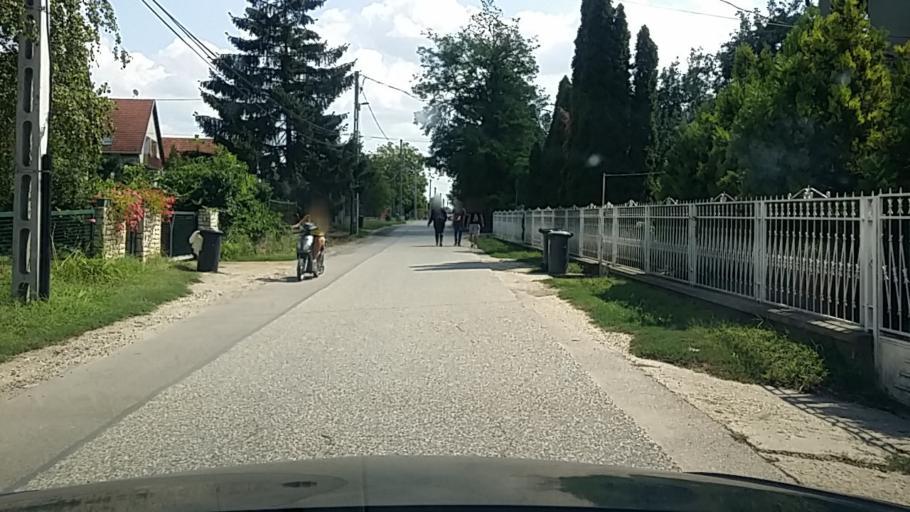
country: HU
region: Pest
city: Halasztelek
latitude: 47.3806
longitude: 19.0125
